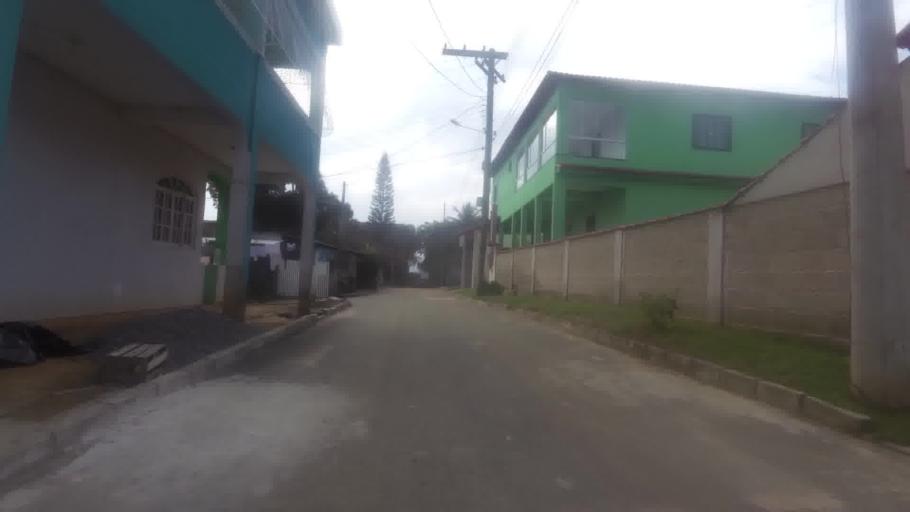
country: BR
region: Espirito Santo
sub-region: Guarapari
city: Guarapari
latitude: -20.7629
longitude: -40.5752
